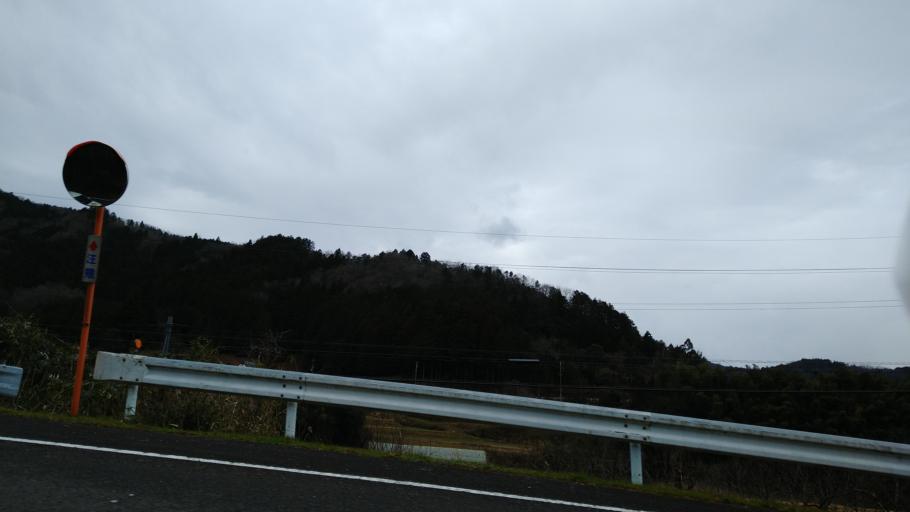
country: JP
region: Kyoto
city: Ayabe
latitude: 35.3312
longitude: 135.3505
